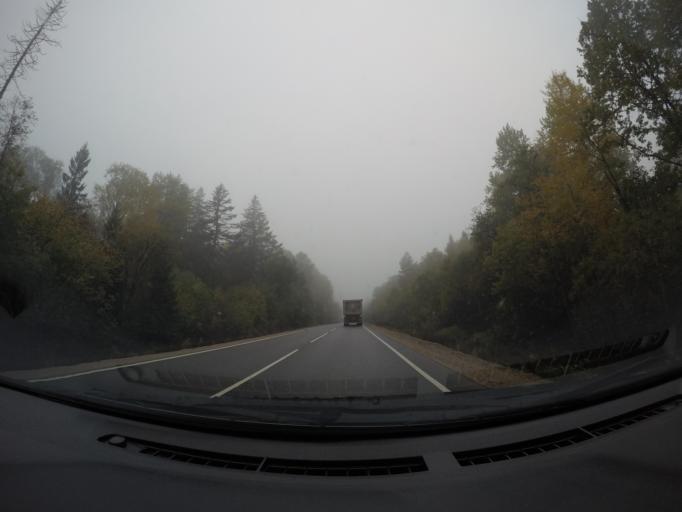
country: RU
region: Moskovskaya
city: Rumyantsevo
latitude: 55.8415
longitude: 36.4720
